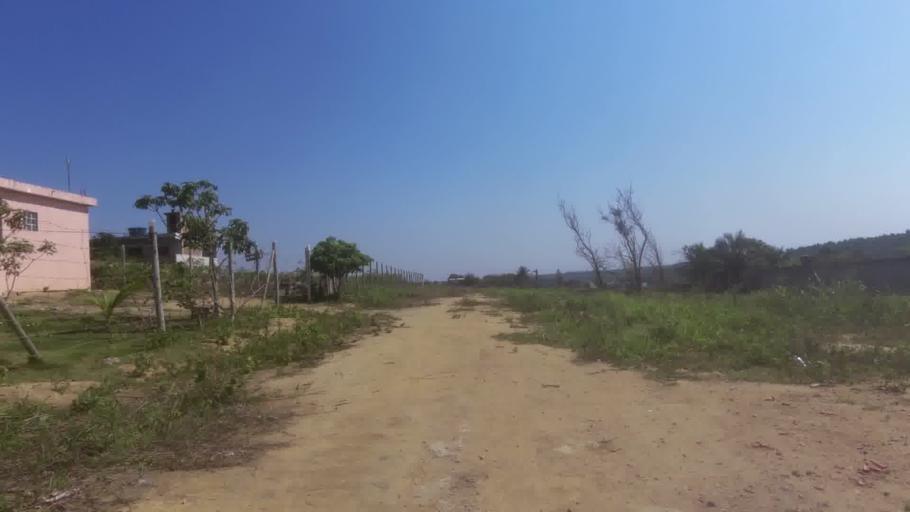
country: BR
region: Espirito Santo
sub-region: Marataizes
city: Marataizes
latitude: -21.1080
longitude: -40.8562
